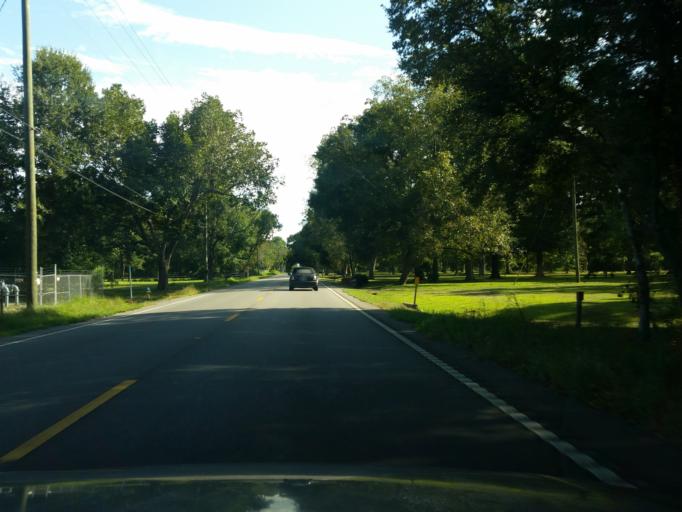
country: US
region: Alabama
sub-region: Mobile County
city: Theodore
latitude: 30.4789
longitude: -88.1132
